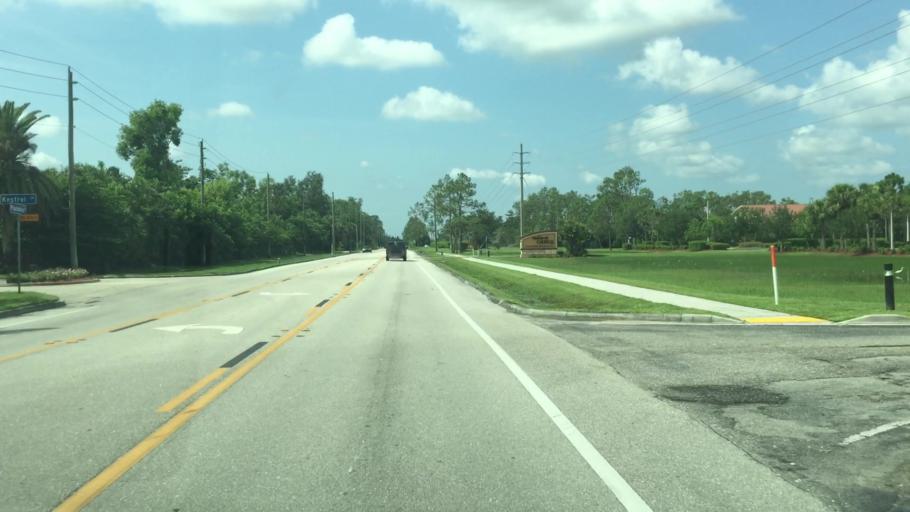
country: US
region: Florida
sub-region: Lee County
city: Villas
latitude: 26.5627
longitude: -81.8470
